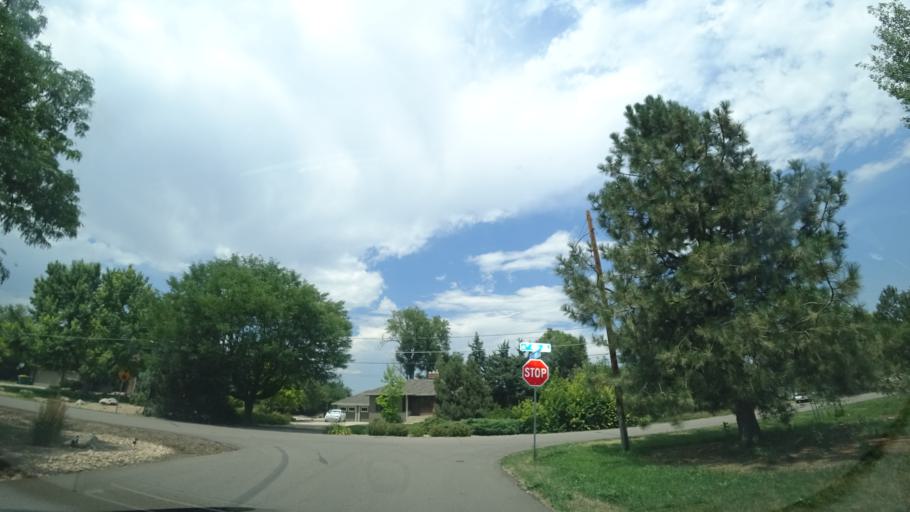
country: US
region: Colorado
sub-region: Jefferson County
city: Lakewood
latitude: 39.7219
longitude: -105.0895
